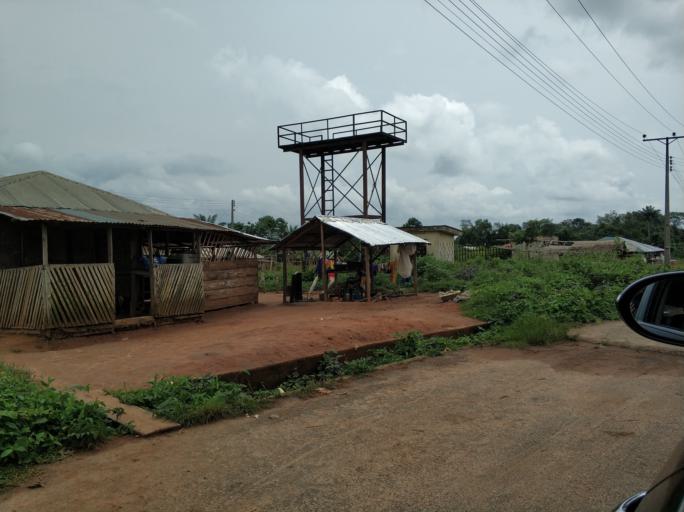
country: NG
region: Ogun
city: Abigi
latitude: 6.6125
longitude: 4.5430
